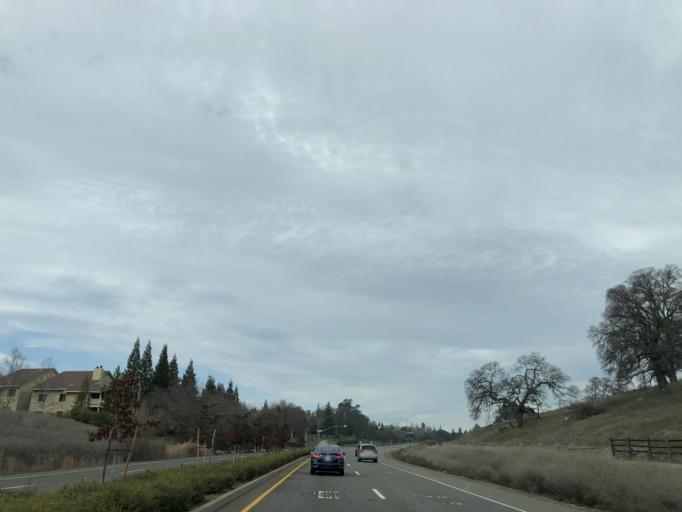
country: US
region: California
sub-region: El Dorado County
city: El Dorado Hills
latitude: 38.6734
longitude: -121.0775
